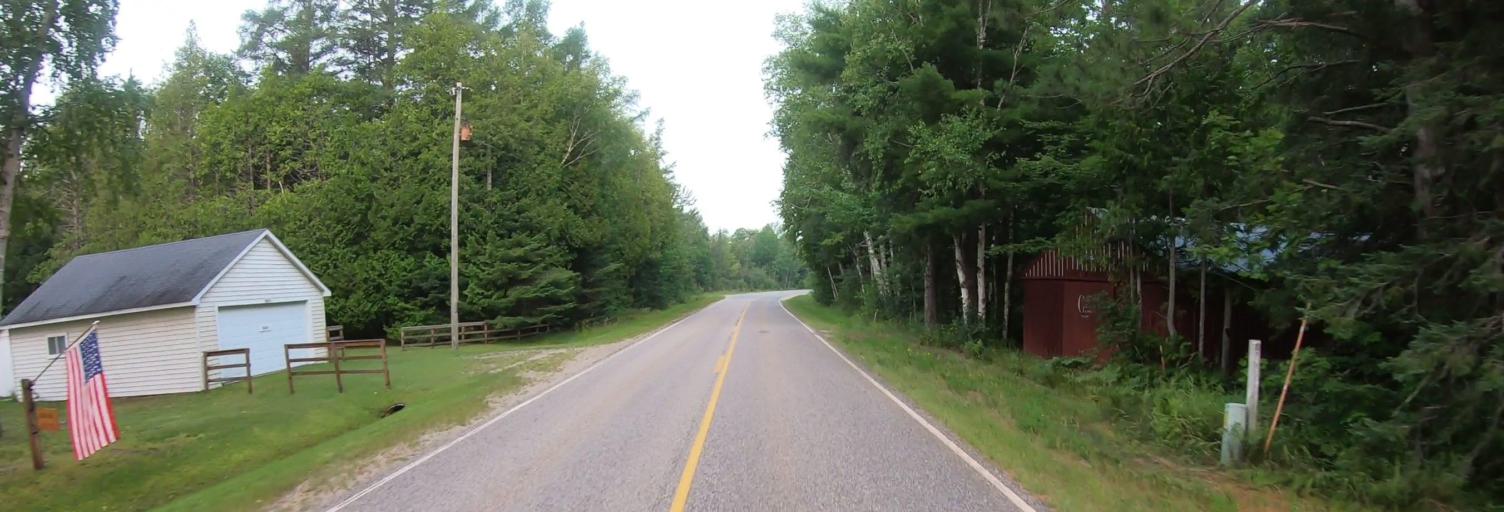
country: US
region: Michigan
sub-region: Chippewa County
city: Sault Ste. Marie
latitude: 46.4649
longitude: -84.9044
